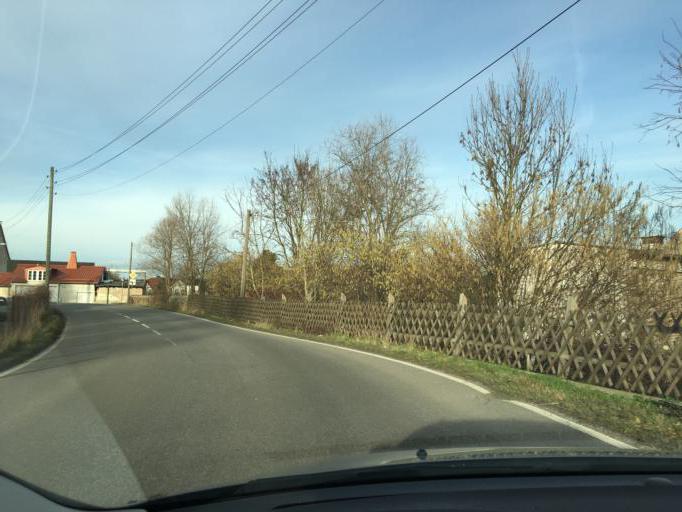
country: DE
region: Thuringia
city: Nobitz
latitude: 51.0028
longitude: 12.4746
